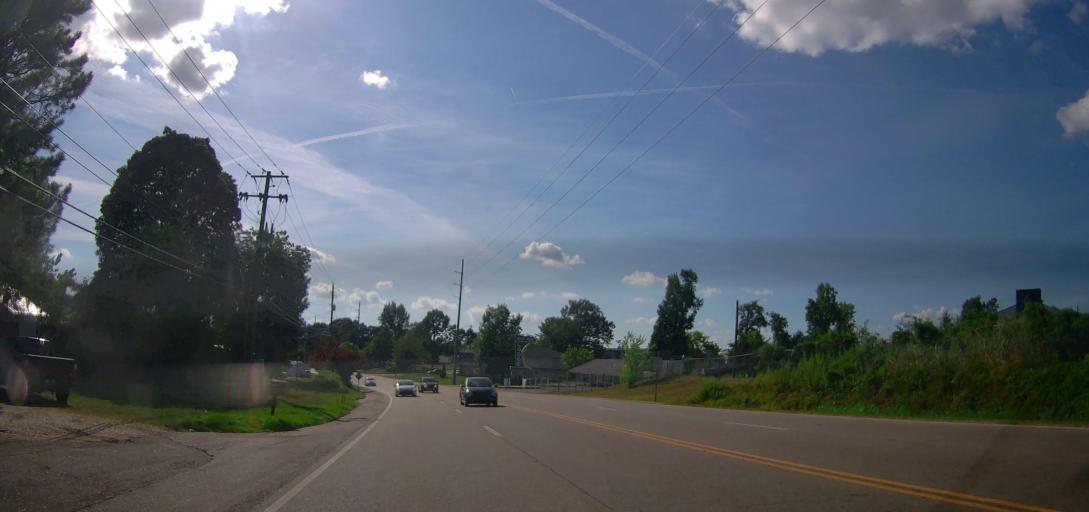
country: US
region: Alabama
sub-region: Tuscaloosa County
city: Holt
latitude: 33.2060
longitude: -87.4913
